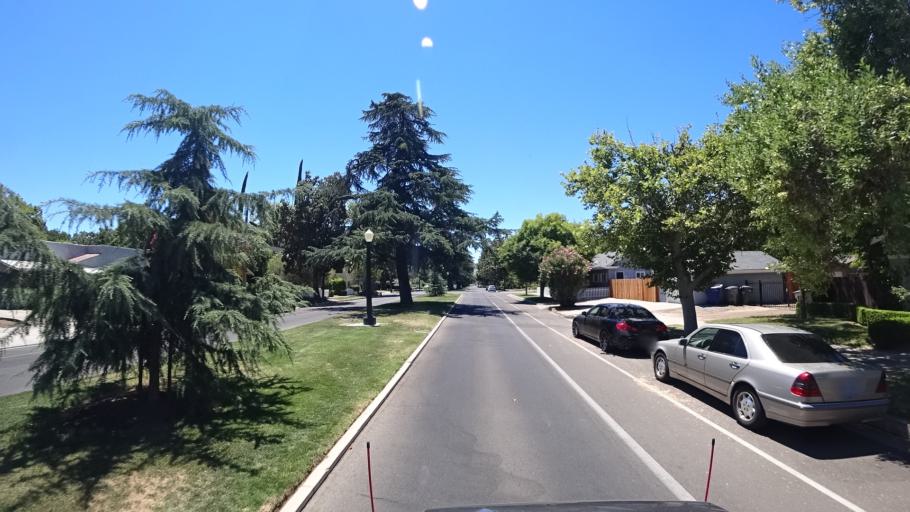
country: US
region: California
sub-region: Fresno County
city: Fresno
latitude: 36.7747
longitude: -119.8042
